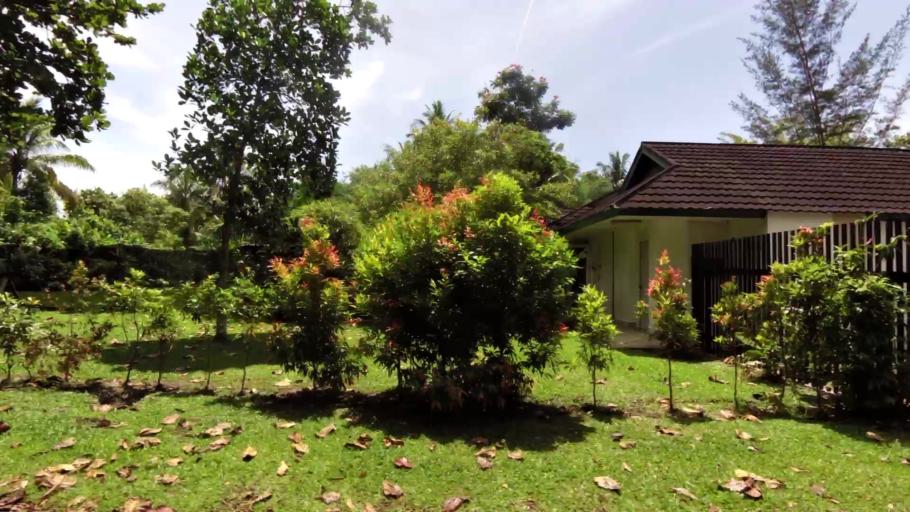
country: BN
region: Belait
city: Kuala Belait
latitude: 4.5982
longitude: 114.2681
